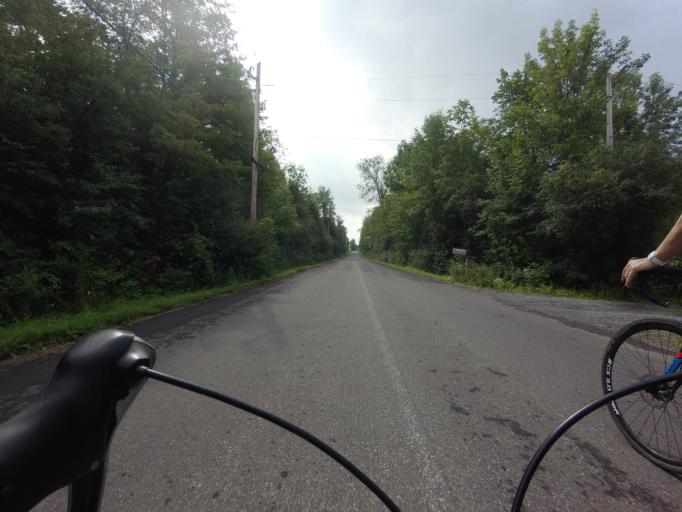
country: CA
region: Ontario
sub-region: Lanark County
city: Smiths Falls
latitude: 44.9616
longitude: -75.8070
